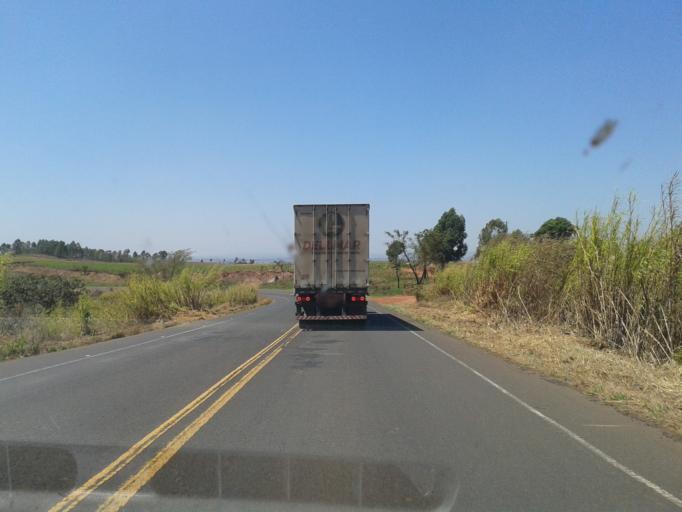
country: BR
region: Minas Gerais
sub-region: Araxa
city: Araxa
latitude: -19.4233
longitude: -47.2464
